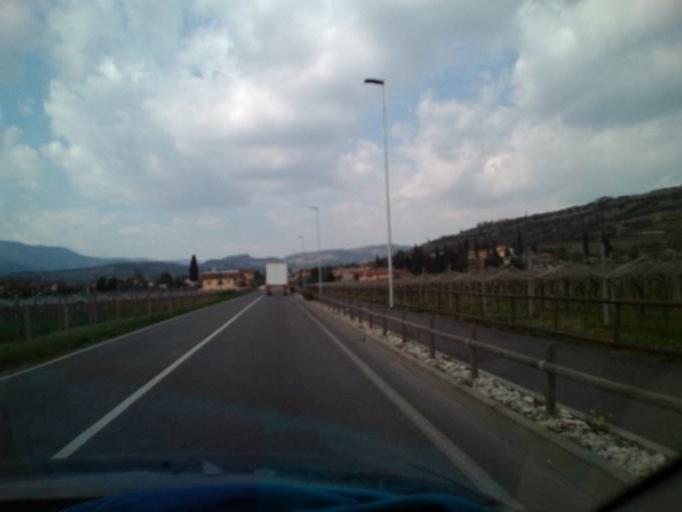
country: IT
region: Veneto
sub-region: Provincia di Verona
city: Pedemonte
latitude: 45.5118
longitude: 10.9137
